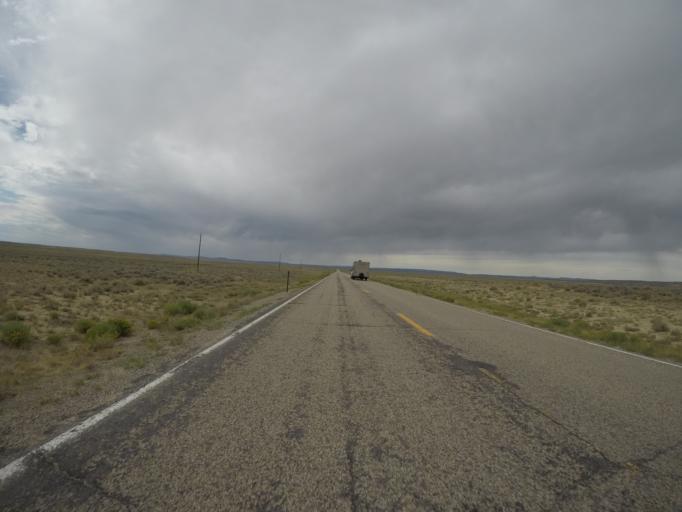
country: US
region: Wyoming
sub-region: Lincoln County
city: Kemmerer
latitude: 41.9625
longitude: -110.1112
